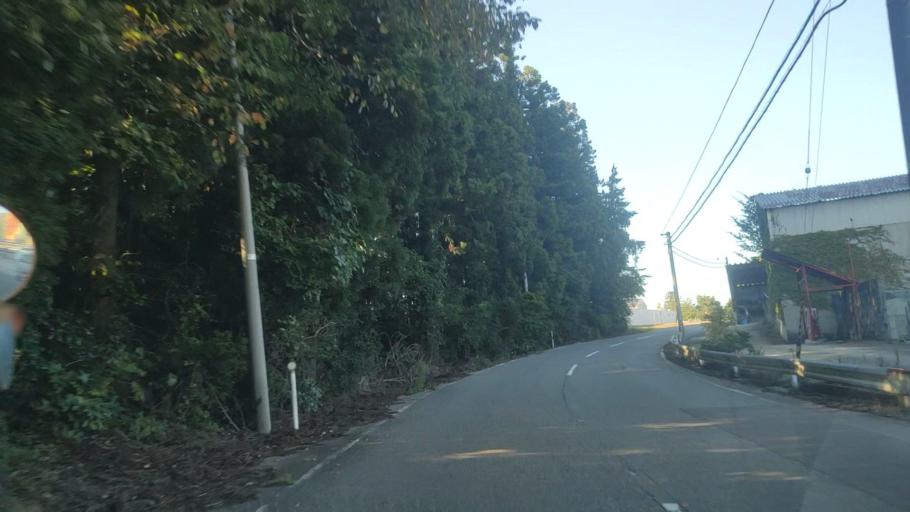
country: JP
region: Ishikawa
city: Nanao
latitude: 37.1271
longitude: 136.9314
